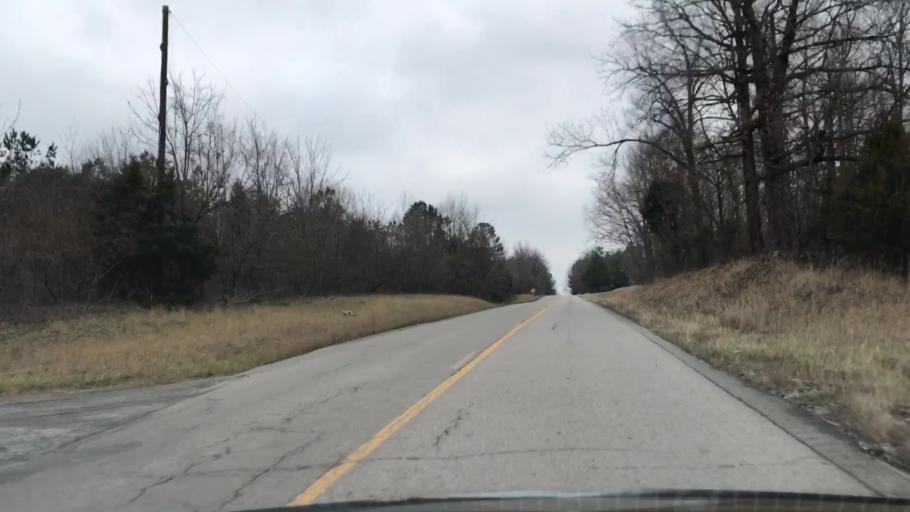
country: US
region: Kentucky
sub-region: Muhlenberg County
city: Morehead
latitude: 37.2800
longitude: -87.2089
